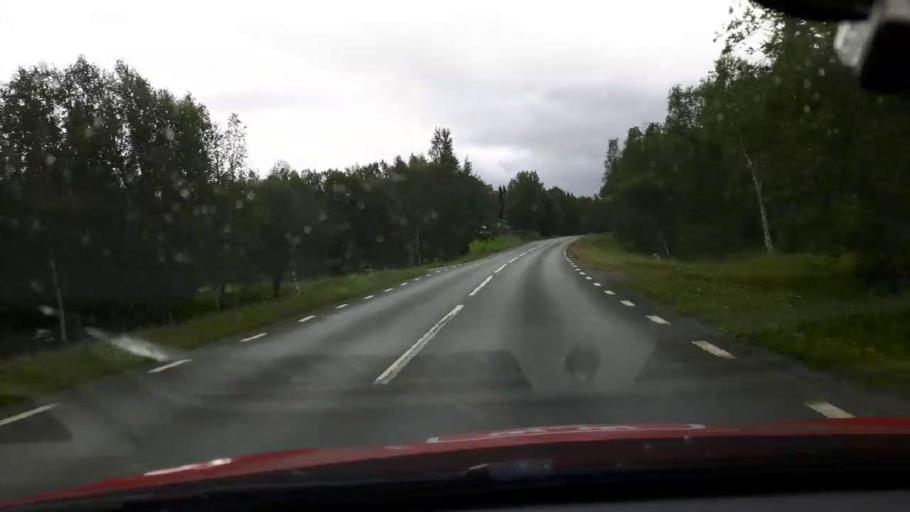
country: SE
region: Jaemtland
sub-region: Are Kommun
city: Are
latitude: 63.3605
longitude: 12.6914
